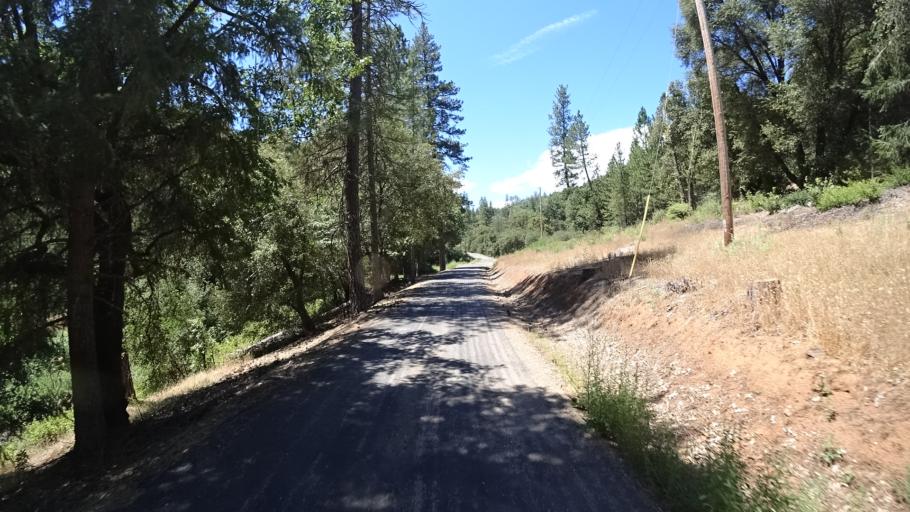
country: US
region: California
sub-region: Calaveras County
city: Forest Meadows
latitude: 38.2140
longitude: -120.4327
